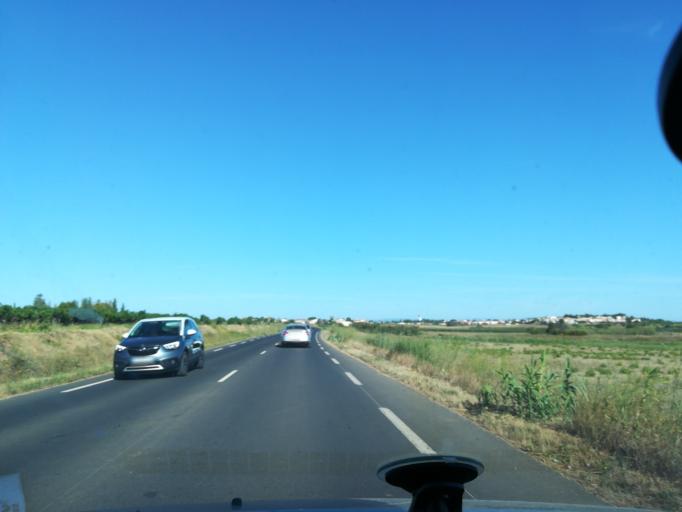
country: FR
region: Languedoc-Roussillon
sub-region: Departement de l'Herault
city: Portiragnes
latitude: 43.2951
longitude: 3.3550
